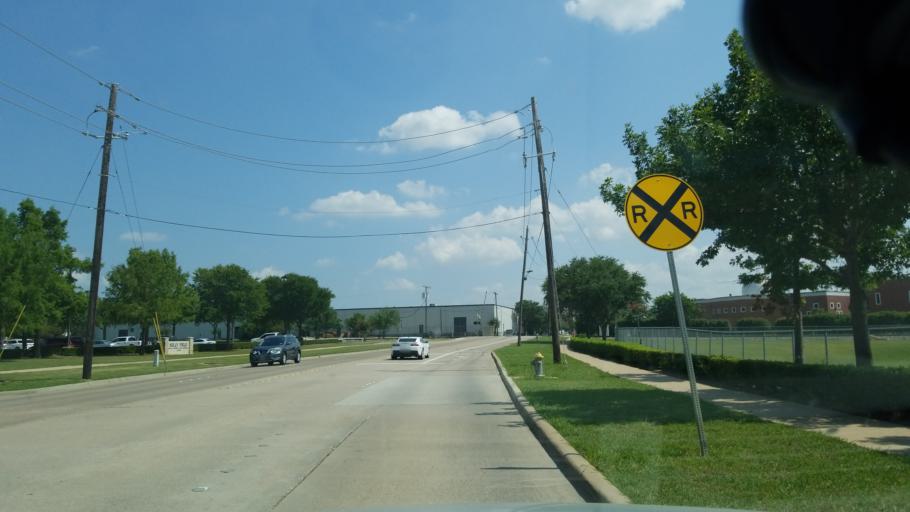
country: US
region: Texas
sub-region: Dallas County
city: Carrollton
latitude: 32.9631
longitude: -96.8771
